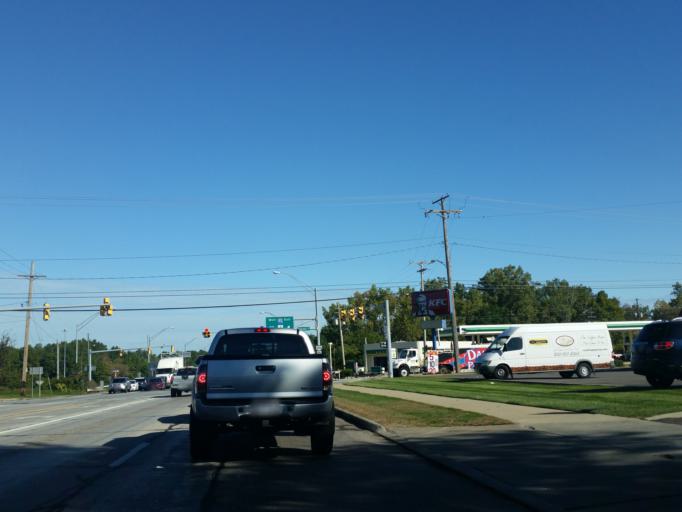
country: US
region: Ohio
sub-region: Cuyahoga County
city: Westlake
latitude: 41.4696
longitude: -81.9016
